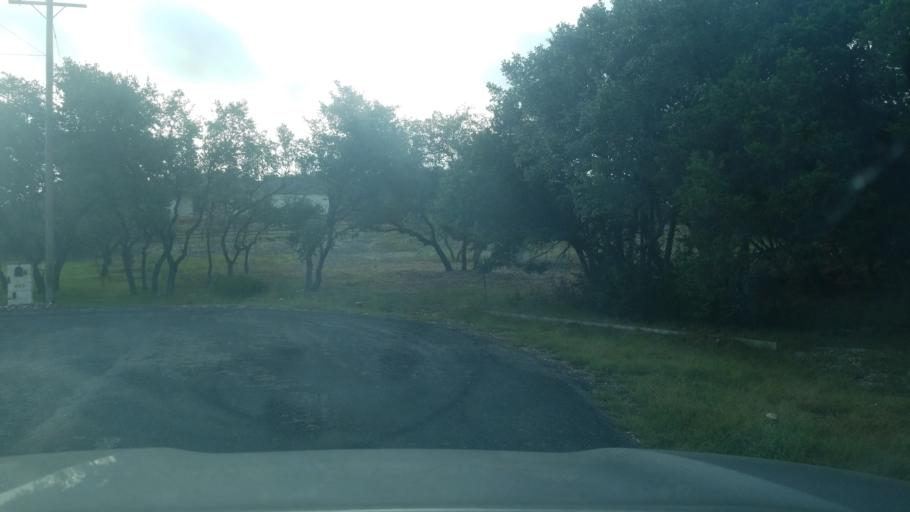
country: US
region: Texas
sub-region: Bexar County
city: Timberwood Park
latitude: 29.7011
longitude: -98.4994
